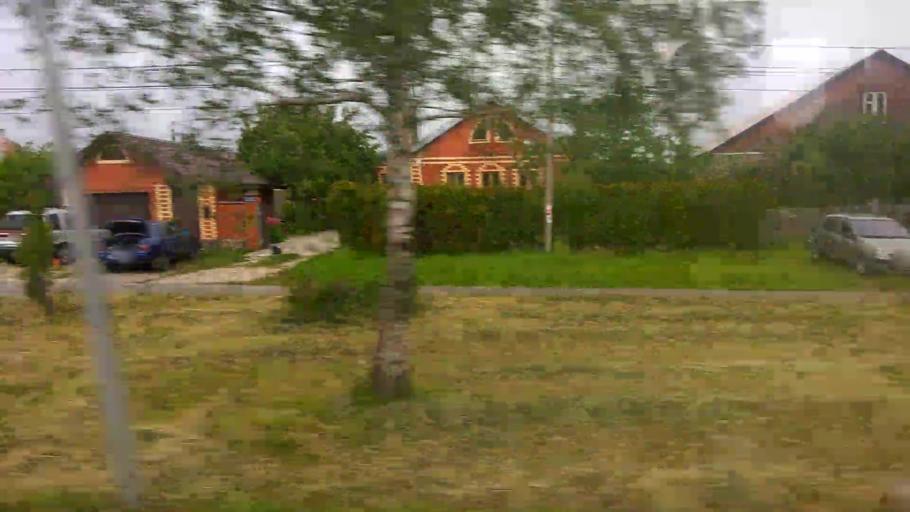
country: RU
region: Moskovskaya
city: Lukhovitsy
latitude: 54.9367
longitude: 39.0123
